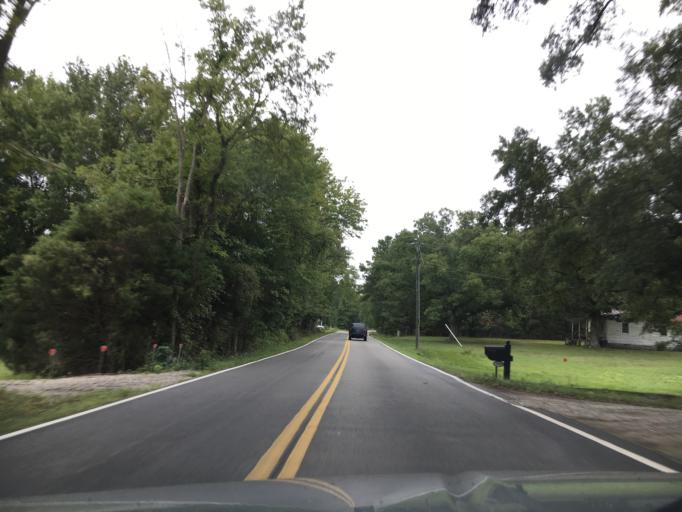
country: US
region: Virginia
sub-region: Powhatan County
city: Powhatan
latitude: 37.4704
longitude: -77.8061
